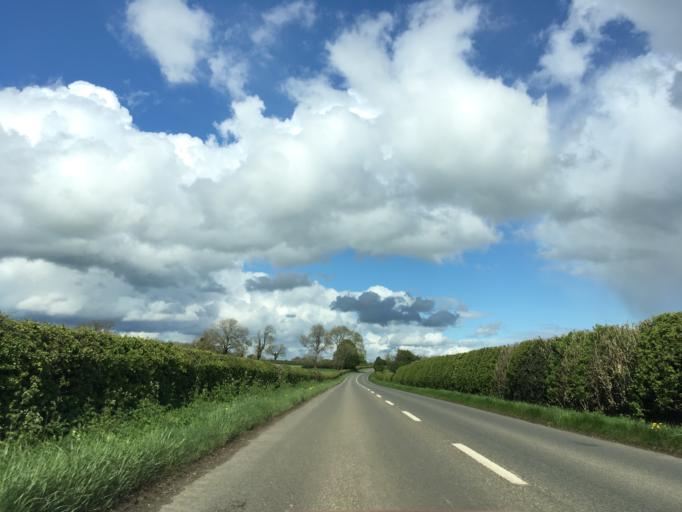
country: GB
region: England
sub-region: Gloucestershire
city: Tetbury
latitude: 51.6143
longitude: -2.1949
